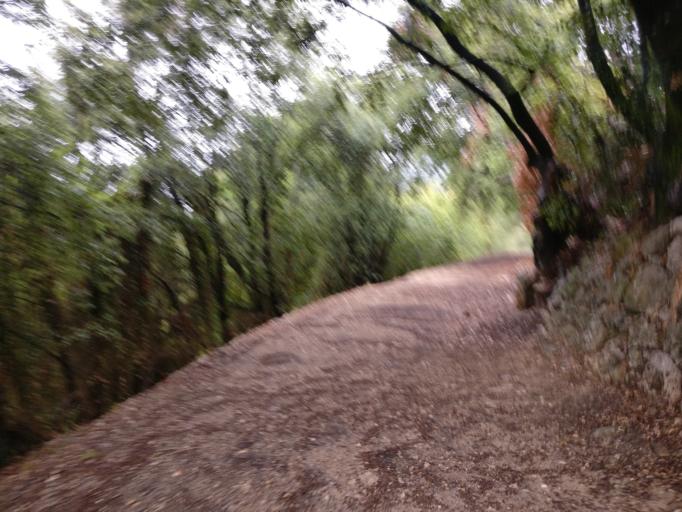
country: FR
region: Provence-Alpes-Cote d'Azur
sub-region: Departement des Alpes-Maritimes
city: Villefranche-sur-Mer
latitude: 43.7148
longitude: 7.2995
